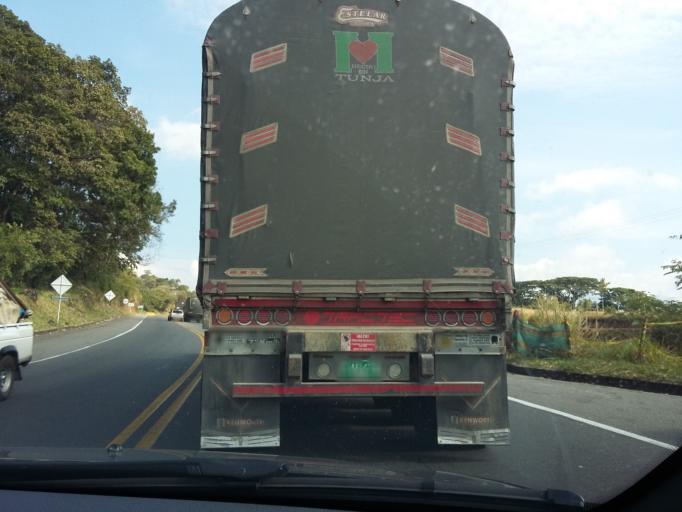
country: CO
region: Tolima
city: Ibague
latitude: 4.4077
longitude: -75.1842
